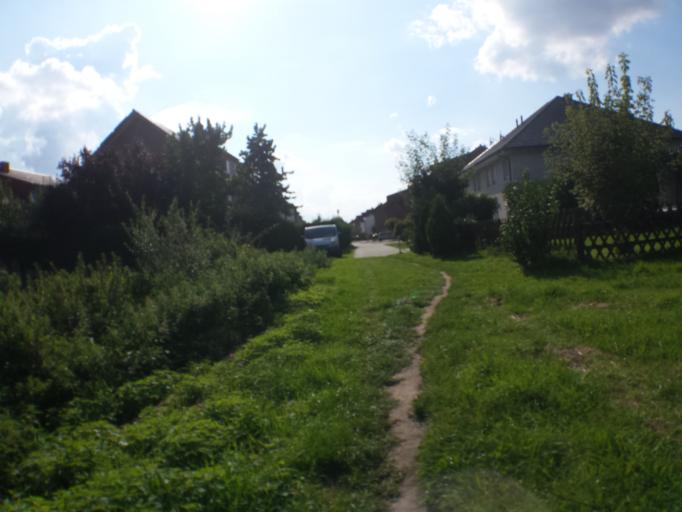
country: DE
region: North Rhine-Westphalia
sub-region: Regierungsbezirk Arnsberg
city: Lippstadt
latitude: 51.6880
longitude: 8.3119
